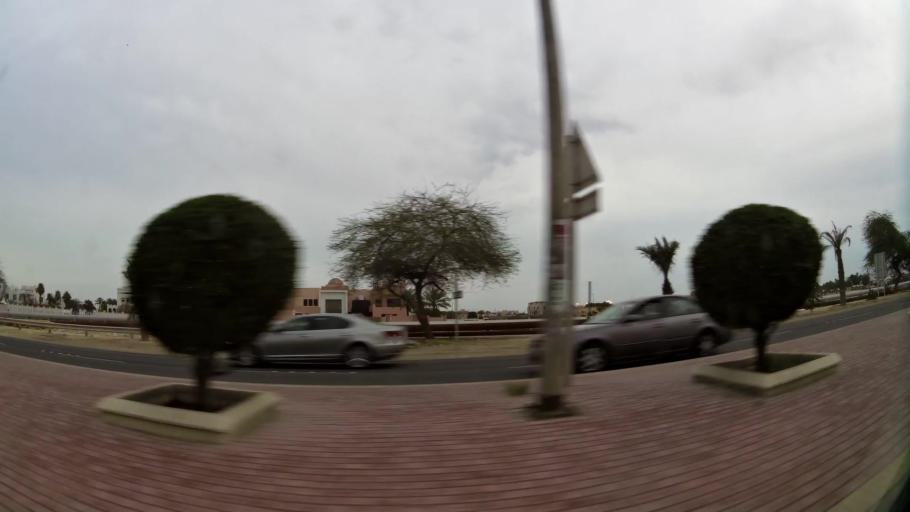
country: BH
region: Northern
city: Ar Rifa'
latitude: 26.1355
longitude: 50.5305
